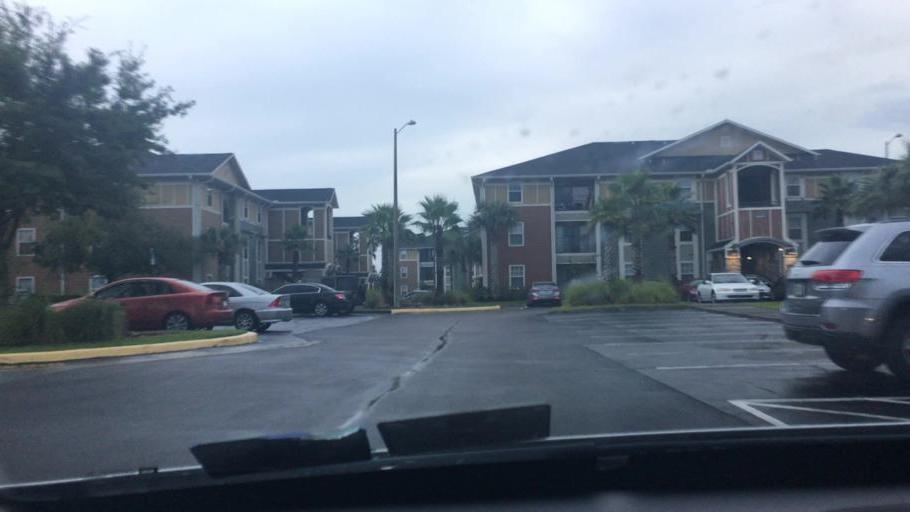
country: US
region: Florida
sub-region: Orange County
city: Alafaya
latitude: 28.6095
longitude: -81.2091
